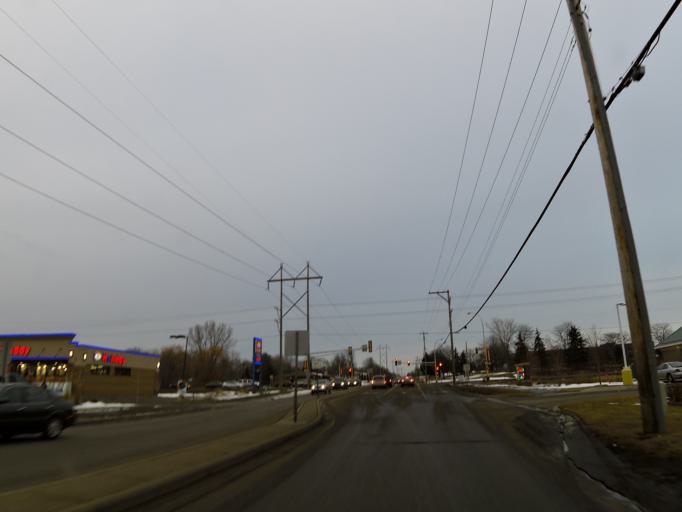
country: US
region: Minnesota
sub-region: Ramsey County
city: North Saint Paul
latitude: 44.9966
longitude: -92.9645
